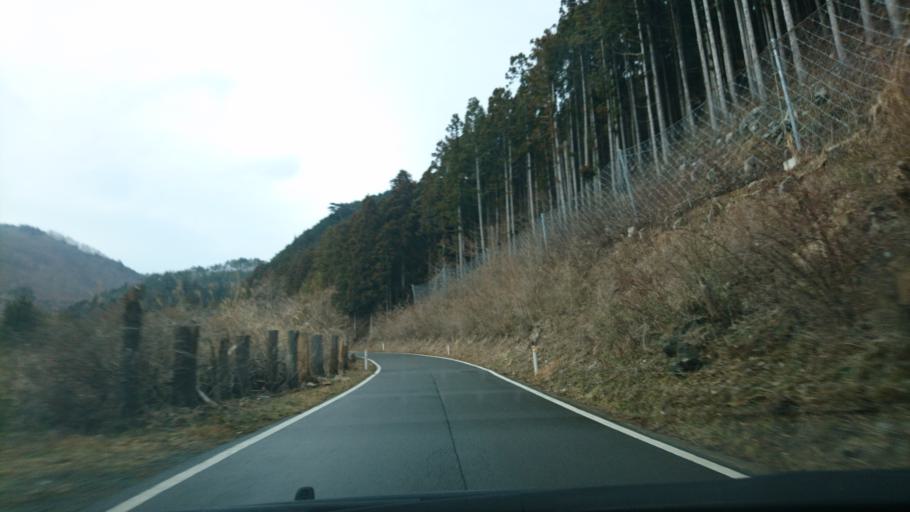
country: JP
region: Iwate
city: Ofunato
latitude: 38.9894
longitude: 141.5521
